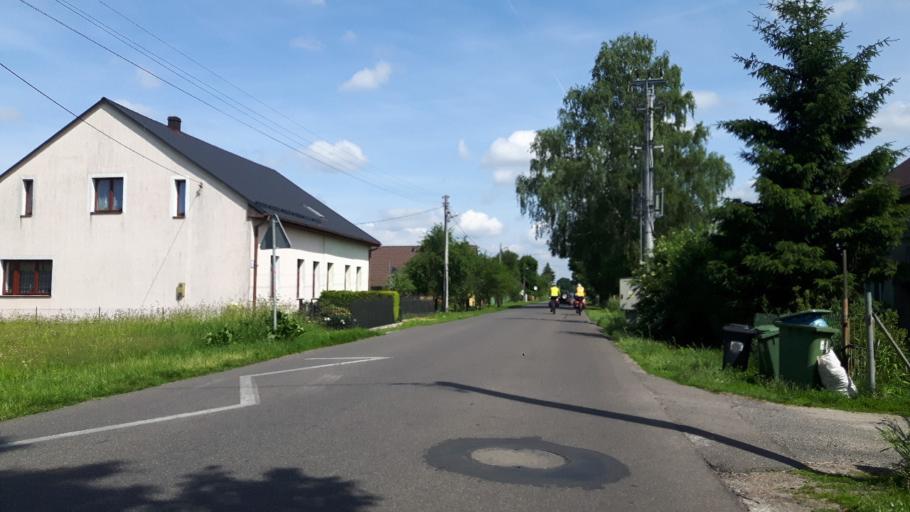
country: PL
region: West Pomeranian Voivodeship
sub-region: Powiat goleniowski
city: Goleniow
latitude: 53.4898
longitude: 14.7769
